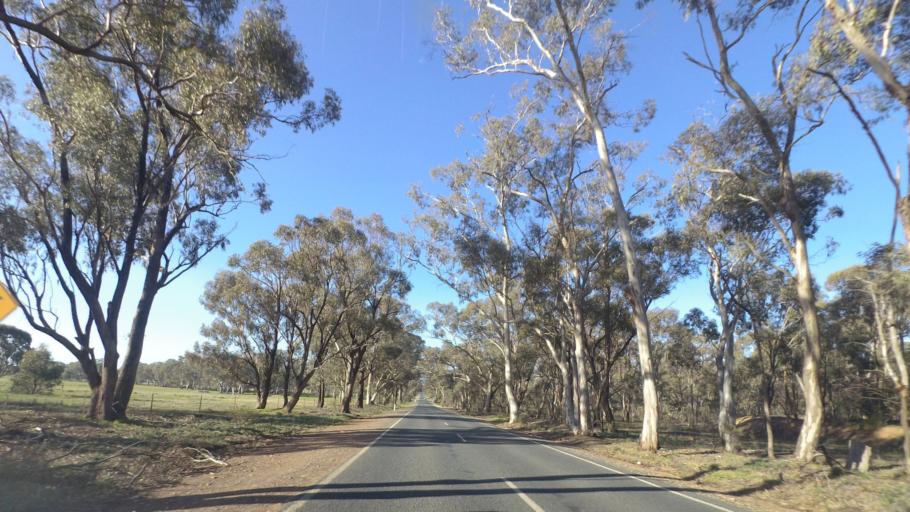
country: AU
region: Victoria
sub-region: Greater Bendigo
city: Epsom
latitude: -36.6760
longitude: 144.3925
